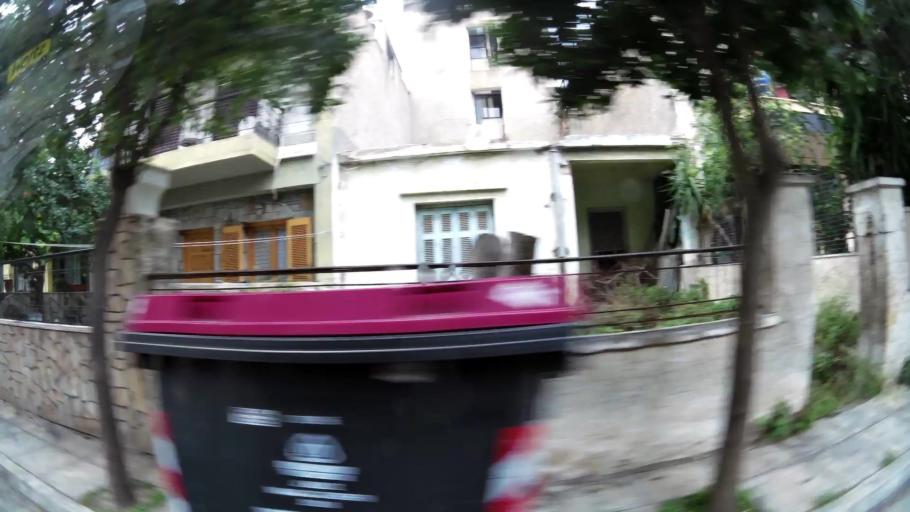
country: GR
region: Attica
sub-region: Nomos Piraios
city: Agios Ioannis Rentis
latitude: 37.9619
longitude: 23.6622
